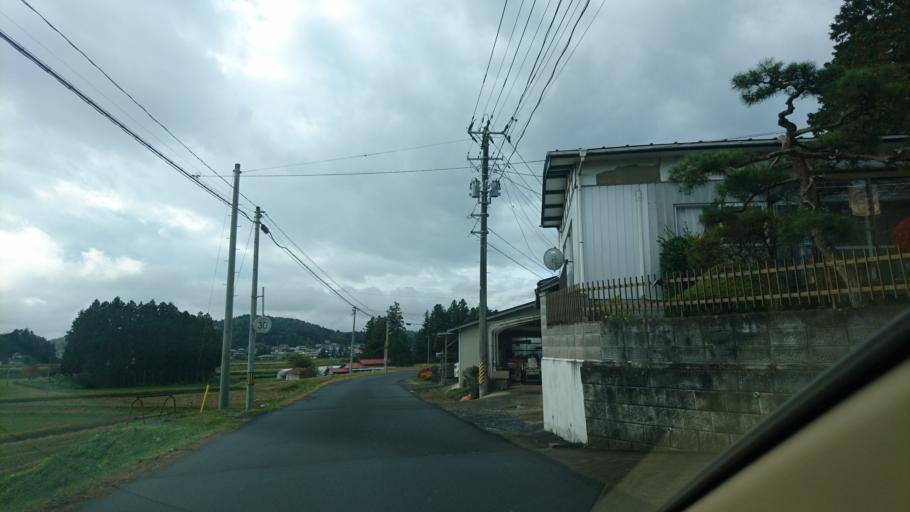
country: JP
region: Iwate
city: Ichinoseki
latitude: 38.7737
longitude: 141.0046
